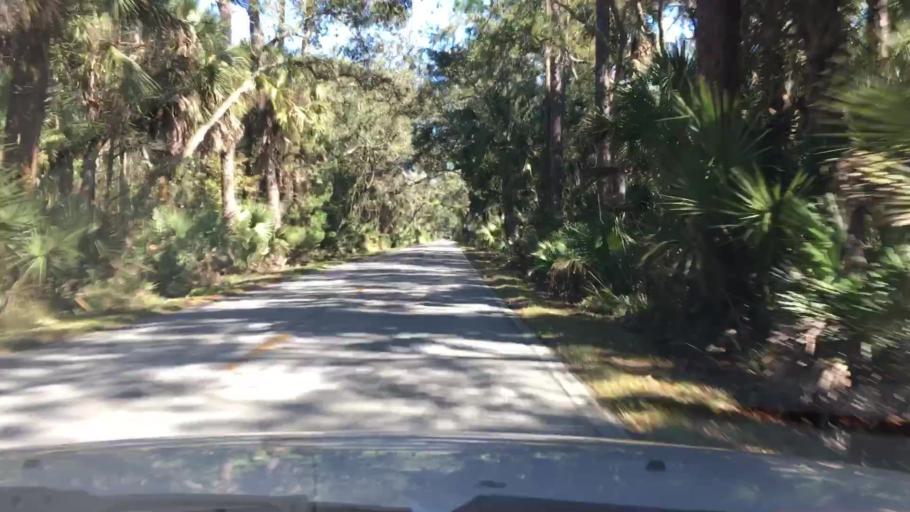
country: US
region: Florida
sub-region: Volusia County
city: Ormond-by-the-Sea
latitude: 29.3419
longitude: -81.0994
